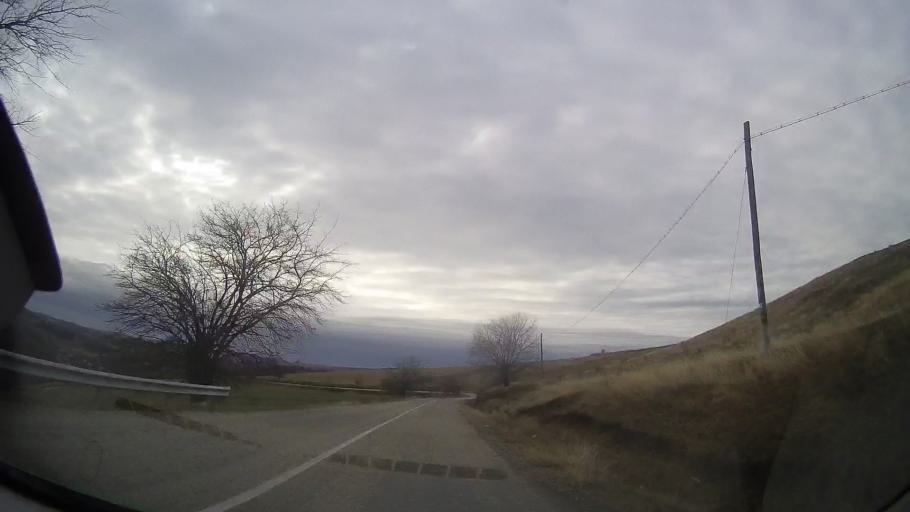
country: RO
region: Bistrita-Nasaud
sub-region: Comuna Budesti
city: Budesti
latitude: 46.8876
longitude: 24.2408
